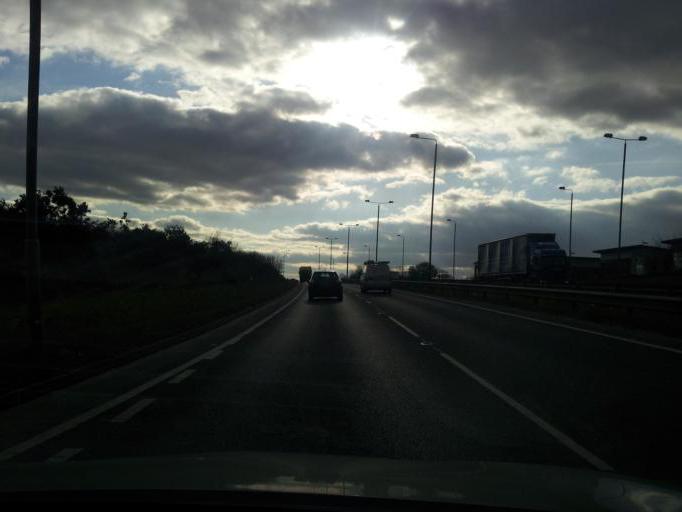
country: GB
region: England
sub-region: Derbyshire
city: Pinxton
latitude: 53.1072
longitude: -1.3171
